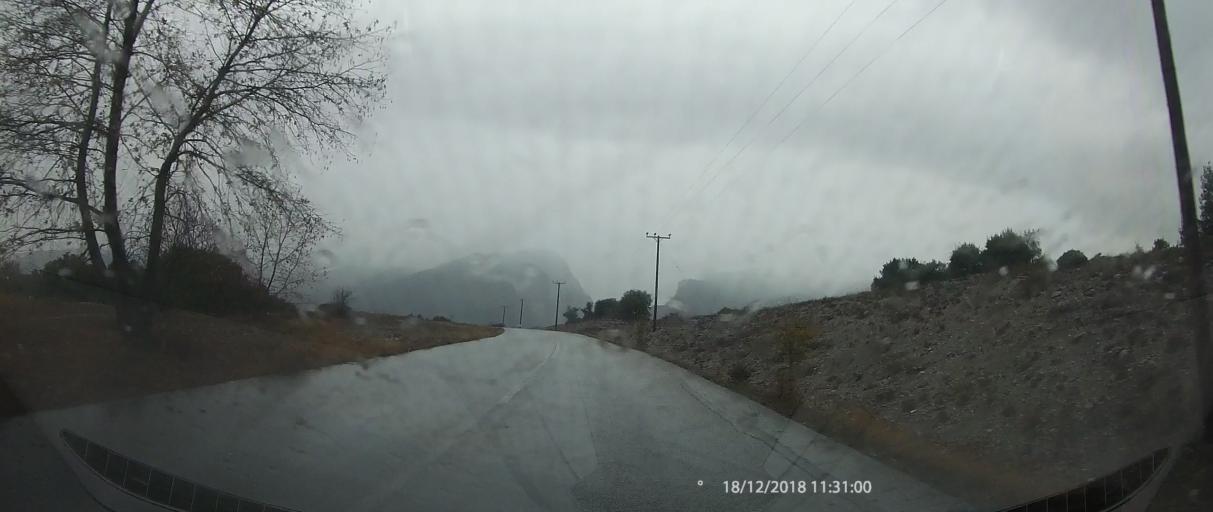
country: GR
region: Central Macedonia
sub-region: Nomos Pierias
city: Litochoro
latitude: 40.1174
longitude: 22.5164
